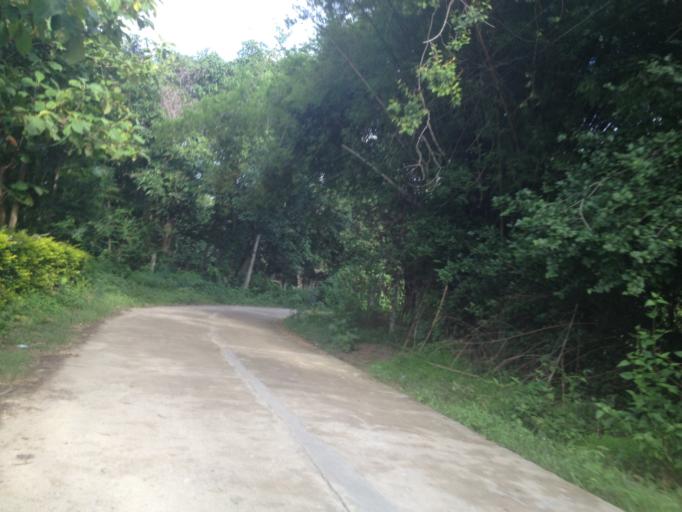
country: TH
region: Chiang Mai
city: Hang Dong
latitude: 18.6843
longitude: 98.8940
